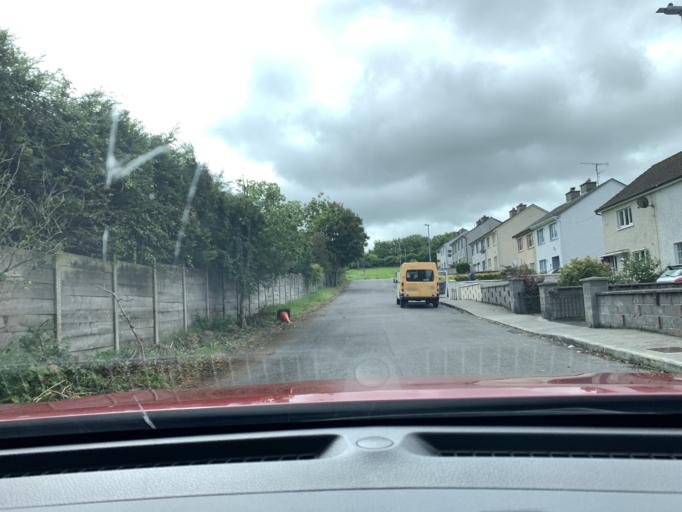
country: IE
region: Connaught
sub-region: Roscommon
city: Boyle
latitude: 53.9706
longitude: -8.2952
